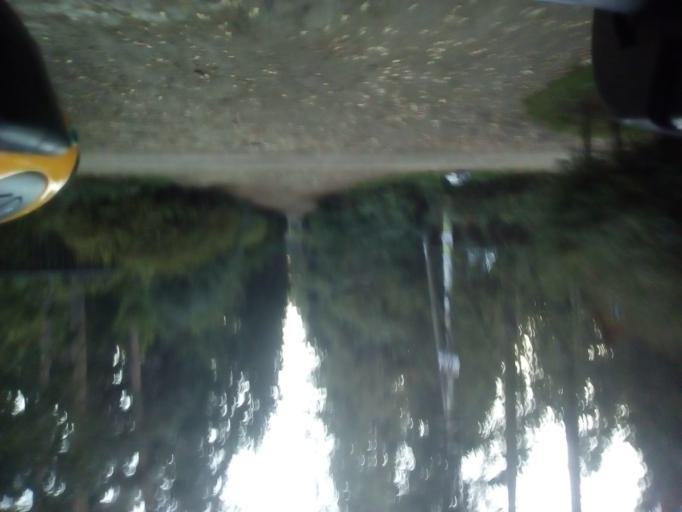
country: RU
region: Moskovskaya
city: Kratovo
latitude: 55.6058
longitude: 38.1713
